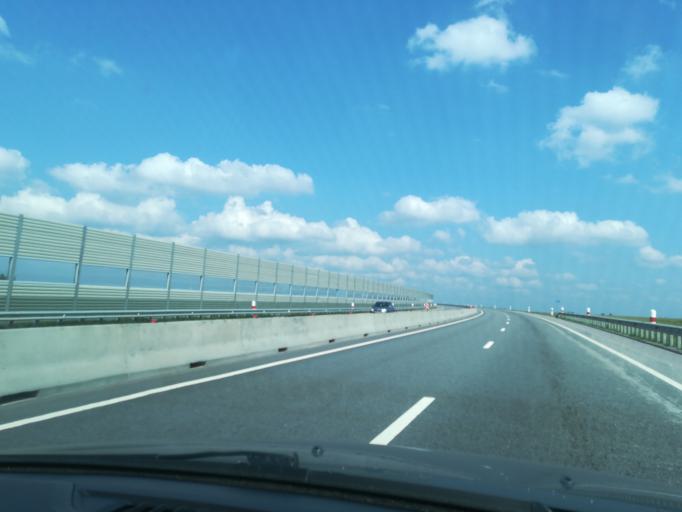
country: RU
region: Leningrad
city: Kingisepp
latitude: 59.5755
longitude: 28.7688
